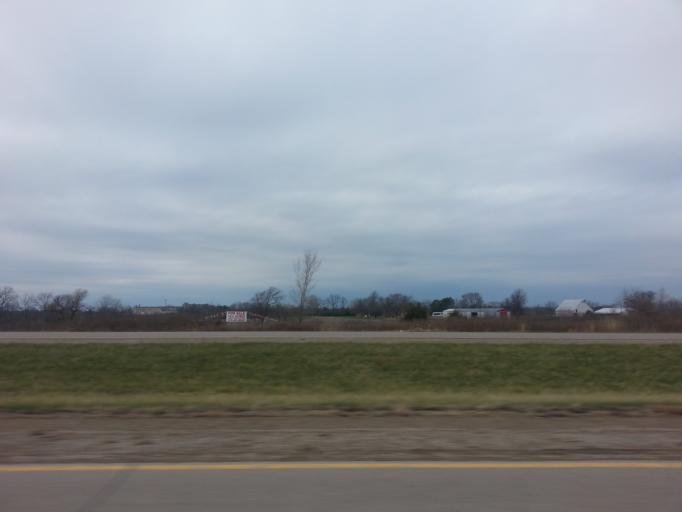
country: US
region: Iowa
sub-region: Henry County
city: Mount Pleasant
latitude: 40.9531
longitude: -91.5234
